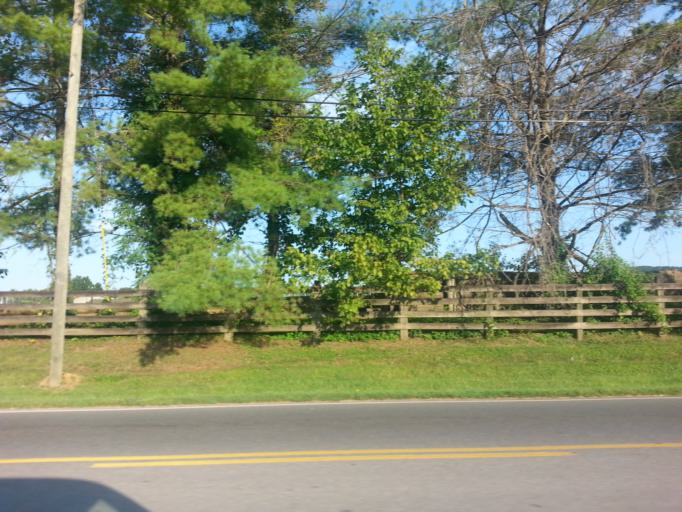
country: US
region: Tennessee
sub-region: Monroe County
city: Sweetwater
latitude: 35.5933
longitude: -84.4679
